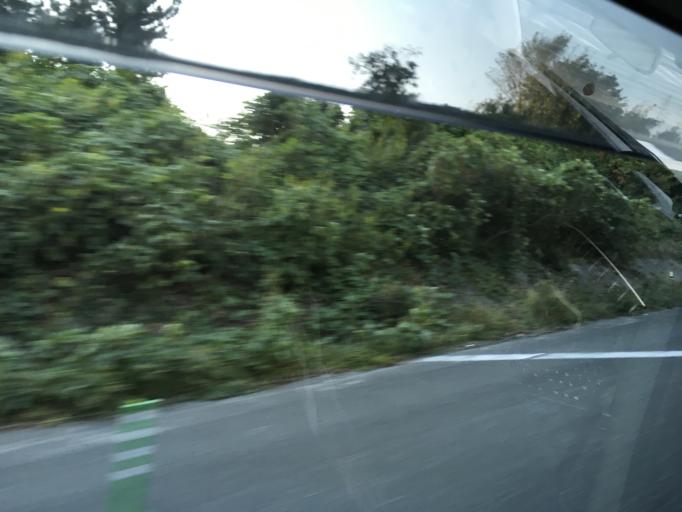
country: JP
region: Miyagi
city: Wakuya
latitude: 38.5706
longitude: 141.2730
